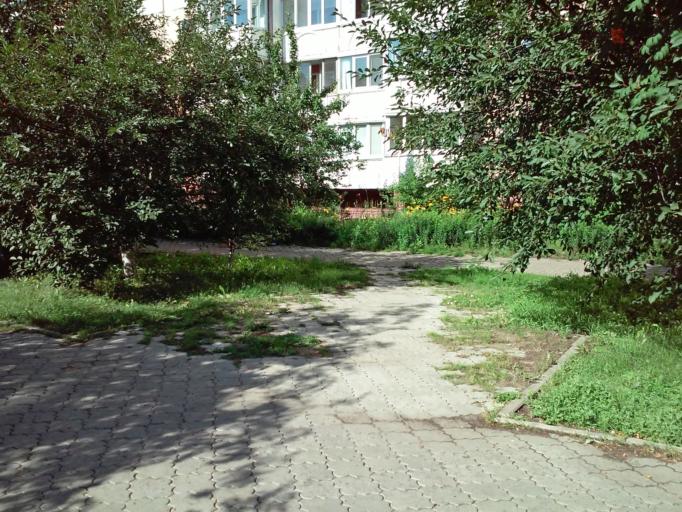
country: RU
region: Belgorod
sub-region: Belgorodskiy Rayon
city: Belgorod
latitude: 50.5567
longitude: 36.5717
